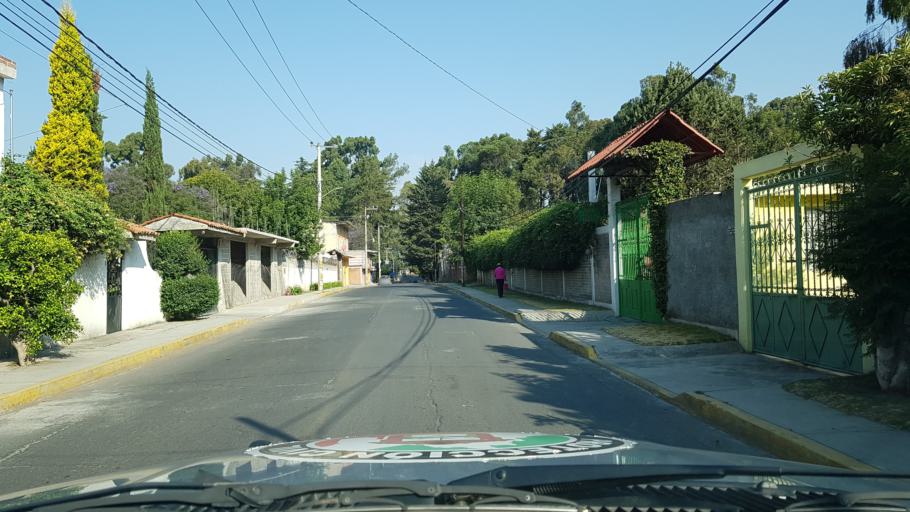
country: MX
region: Mexico
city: Ozumba de Alzate
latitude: 19.0579
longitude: -98.7764
